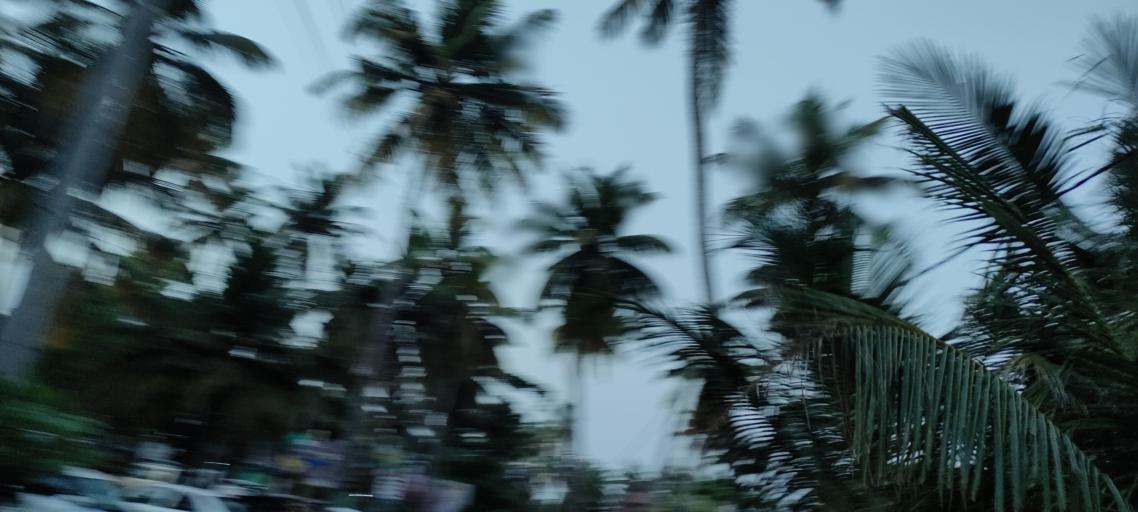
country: IN
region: Kerala
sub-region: Alappuzha
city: Kayankulam
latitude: 9.1337
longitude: 76.4644
